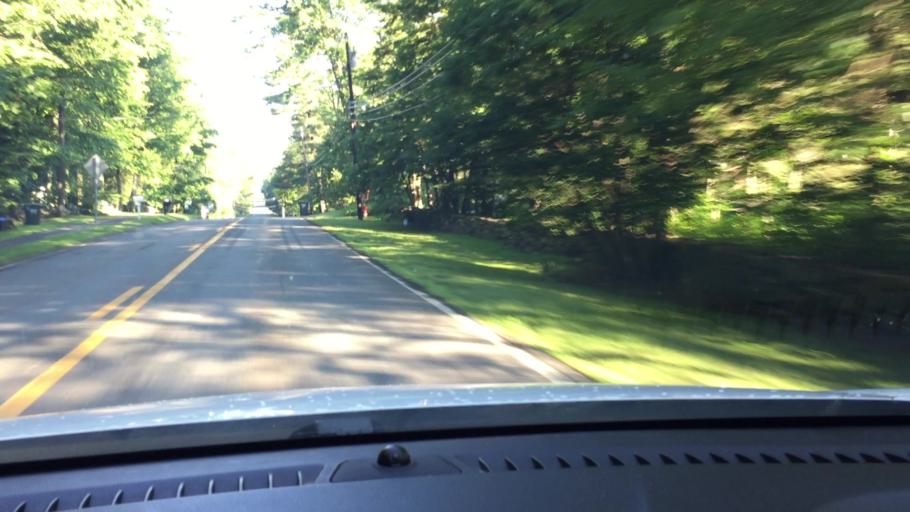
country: US
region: Massachusetts
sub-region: Berkshire County
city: Lenox
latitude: 42.3505
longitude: -73.2739
